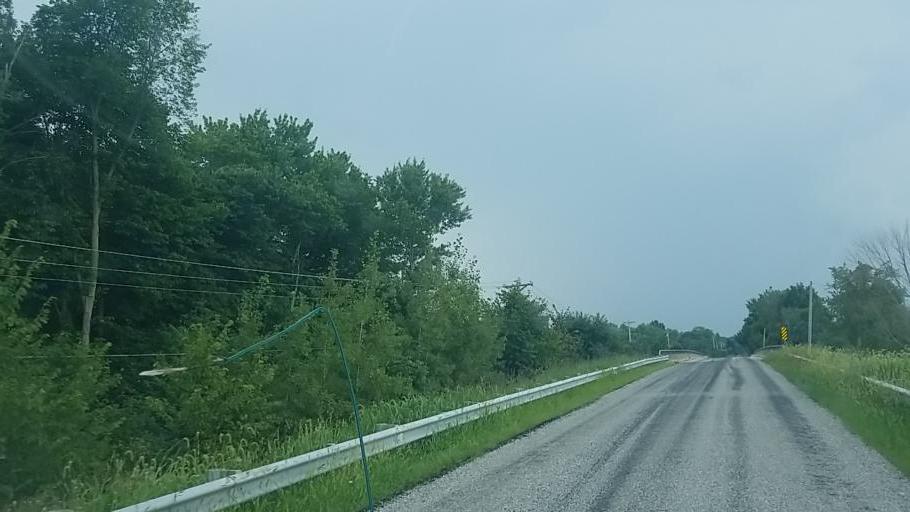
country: US
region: Ohio
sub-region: Medina County
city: Lodi
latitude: 40.9981
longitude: -82.0057
